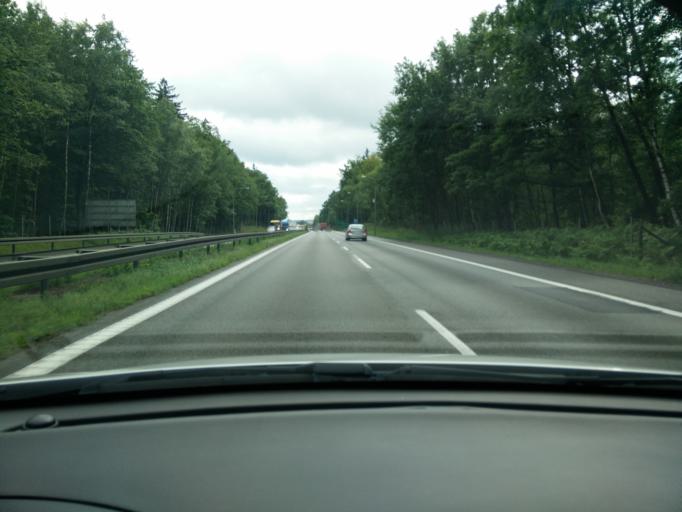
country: PL
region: Pomeranian Voivodeship
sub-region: Gdynia
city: Wielki Kack
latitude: 54.4409
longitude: 18.4894
